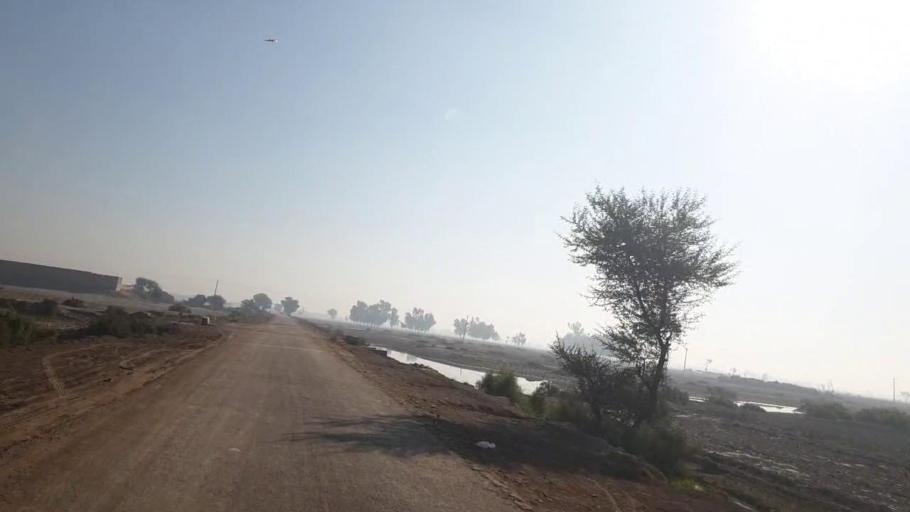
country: PK
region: Sindh
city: Dadu
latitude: 26.6715
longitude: 67.8359
